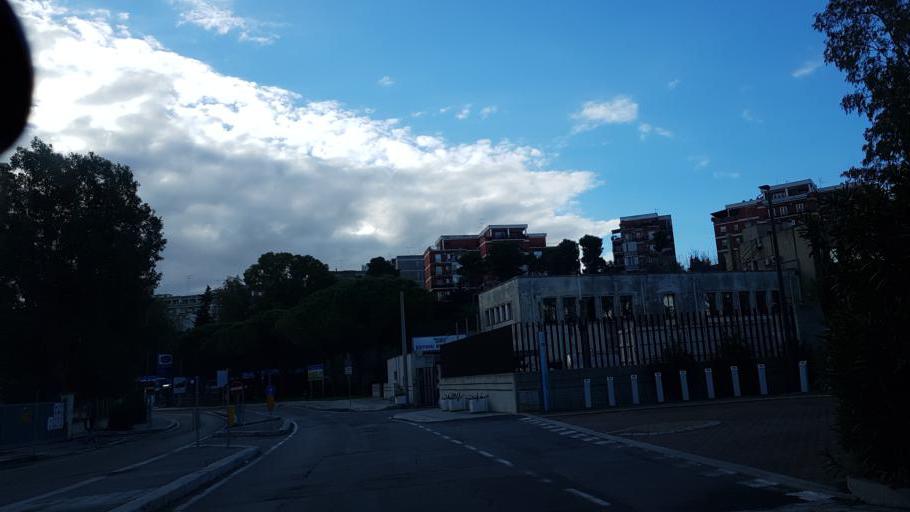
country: IT
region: Apulia
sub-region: Provincia di Brindisi
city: Brindisi
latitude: 40.6397
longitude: 17.9267
